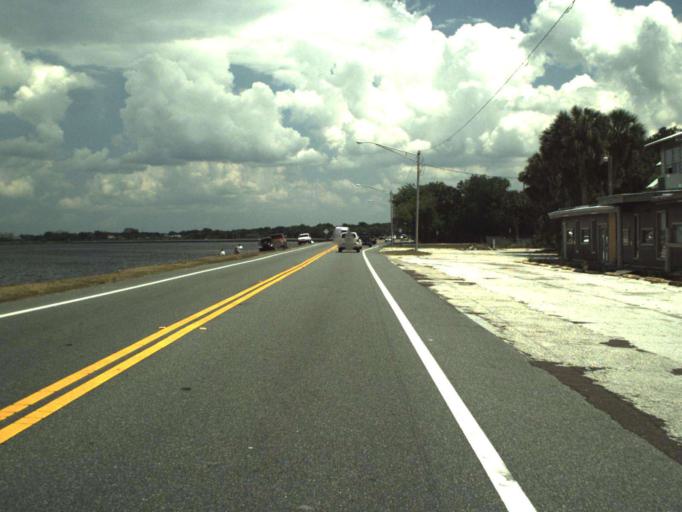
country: US
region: Florida
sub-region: Seminole County
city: Sanford
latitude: 28.8225
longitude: -81.2939
